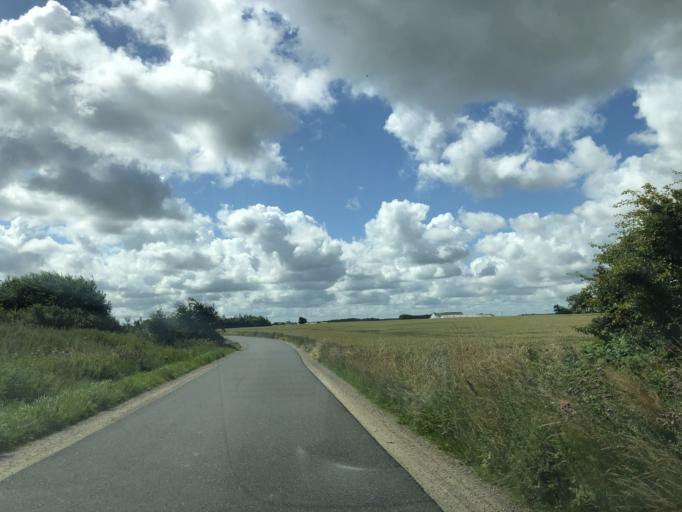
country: DK
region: Central Jutland
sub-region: Struer Kommune
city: Struer
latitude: 56.4729
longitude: 8.5210
